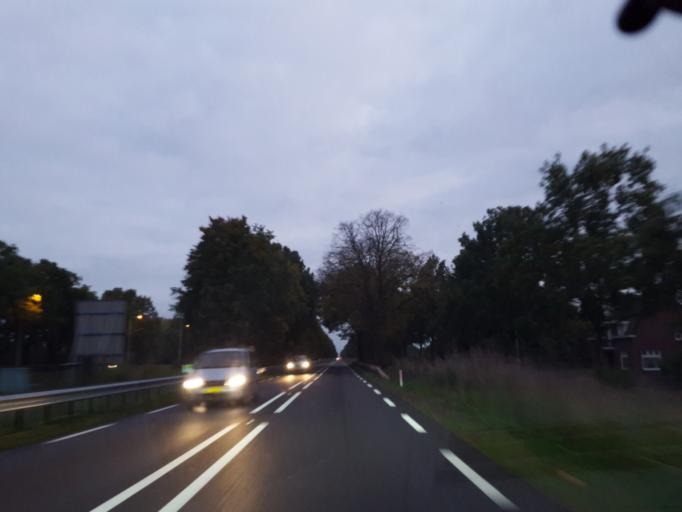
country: NL
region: North Brabant
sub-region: Gemeente Someren
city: Someren
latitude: 51.3500
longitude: 5.7430
